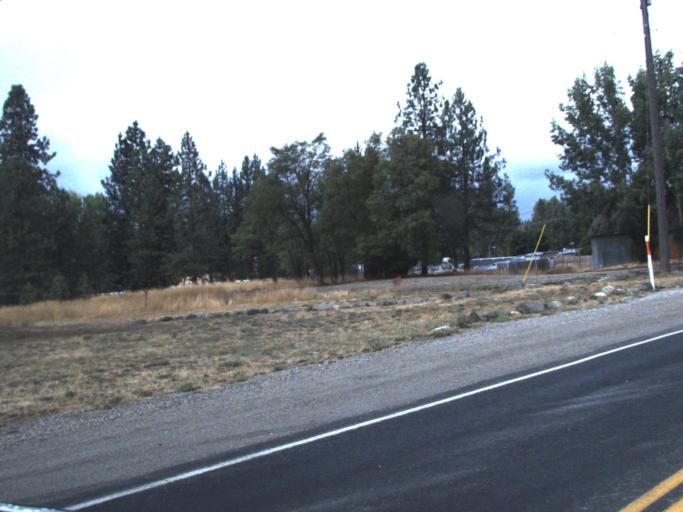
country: US
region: Washington
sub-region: Stevens County
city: Chewelah
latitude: 48.0563
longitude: -117.7413
